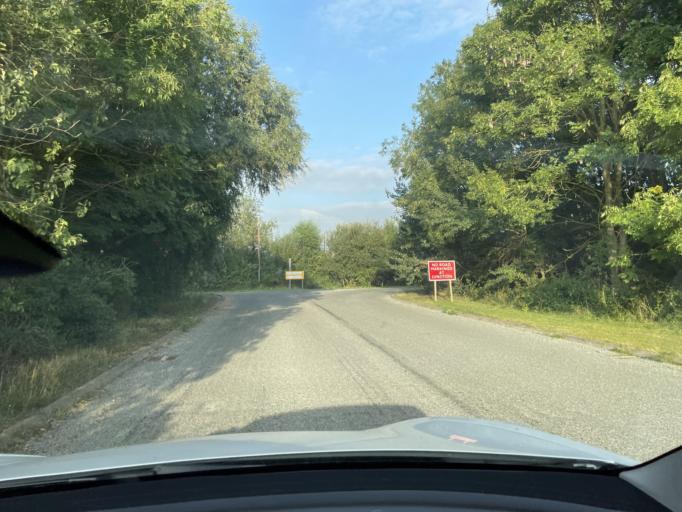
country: GB
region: England
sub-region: Bedford
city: Pertenhall
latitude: 52.3624
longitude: -0.4093
